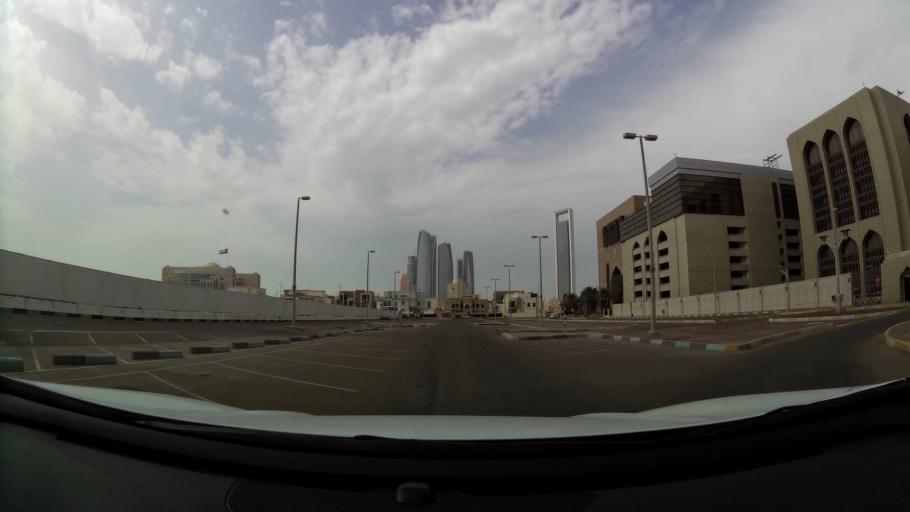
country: AE
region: Abu Dhabi
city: Abu Dhabi
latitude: 24.4557
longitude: 54.3370
